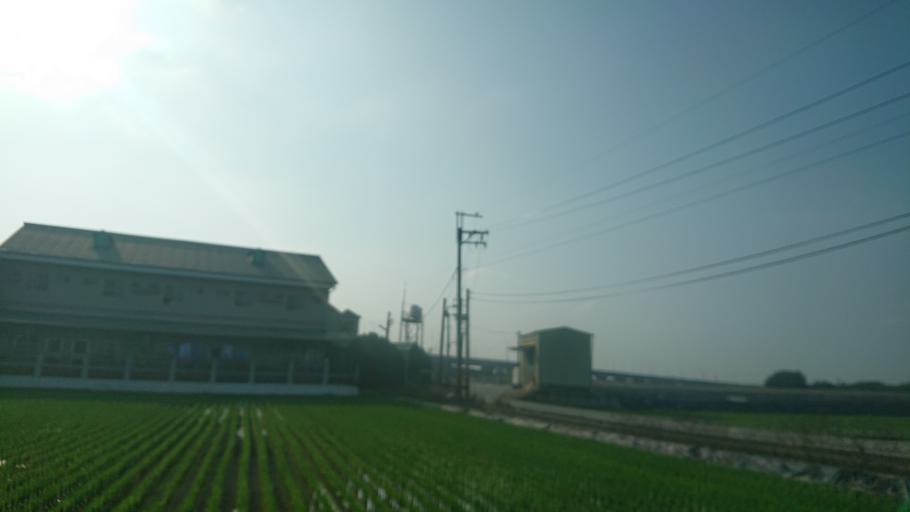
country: TW
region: Taiwan
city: Xinying
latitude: 23.1960
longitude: 120.2717
